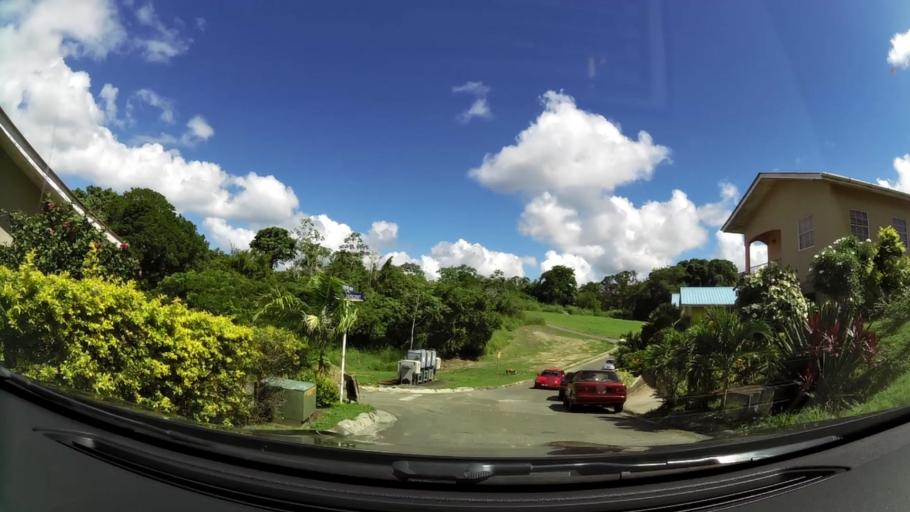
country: TT
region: Tobago
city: Scarborough
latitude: 11.2197
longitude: -60.7689
